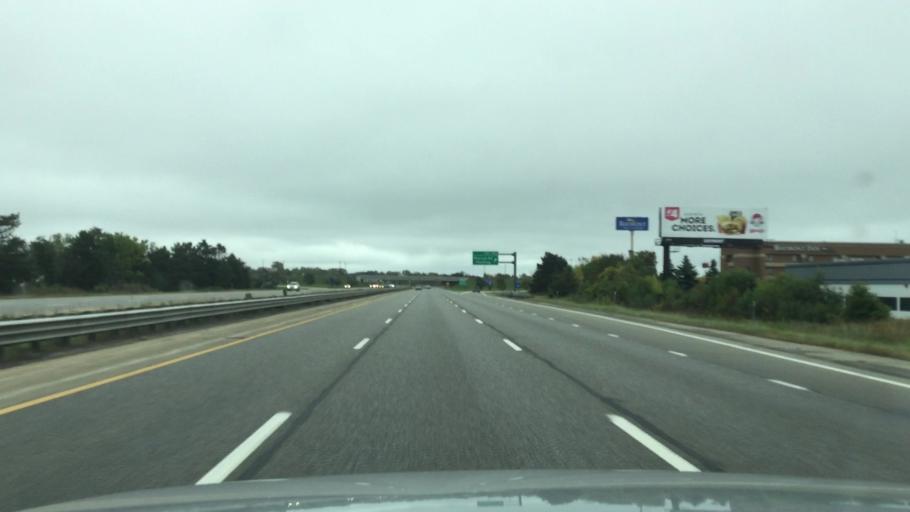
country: US
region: Michigan
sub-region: Genesee County
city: Beecher
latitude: 43.0667
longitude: -83.7627
